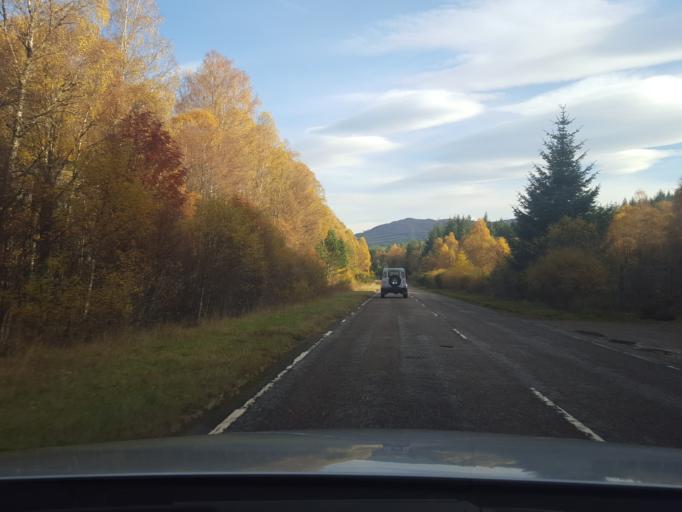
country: GB
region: Scotland
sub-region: Highland
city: Spean Bridge
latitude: 57.1695
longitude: -4.8223
